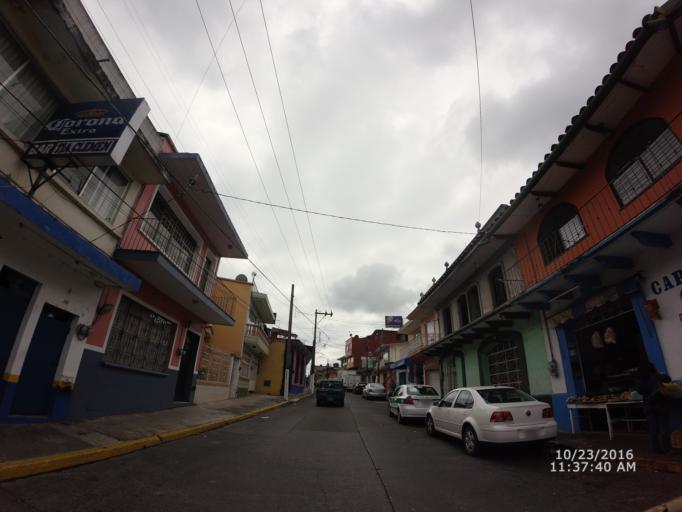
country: MX
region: Veracruz
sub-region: Xalapa
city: Xalapa de Enriquez
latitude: 19.5344
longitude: -96.9281
